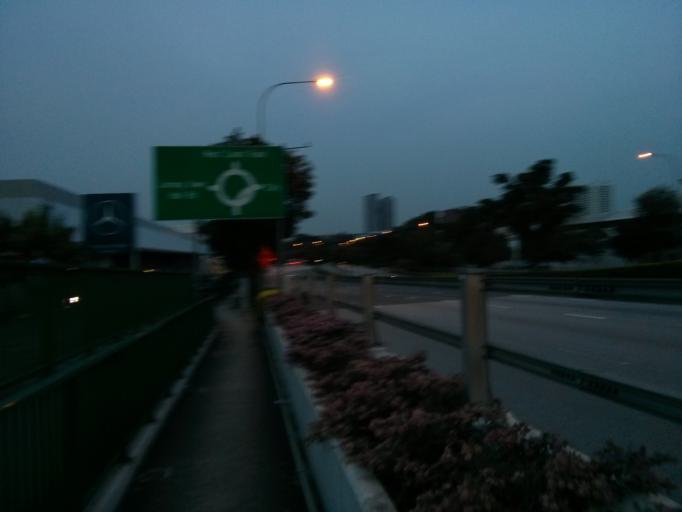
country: SG
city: Singapore
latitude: 1.3080
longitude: 103.7533
